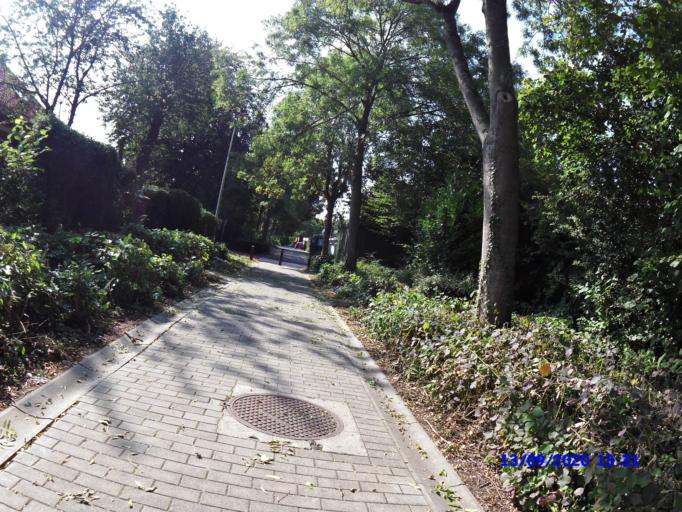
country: BE
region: Flanders
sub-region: Provincie Vlaams-Brabant
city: Dilbeek
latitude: 50.8488
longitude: 4.2584
